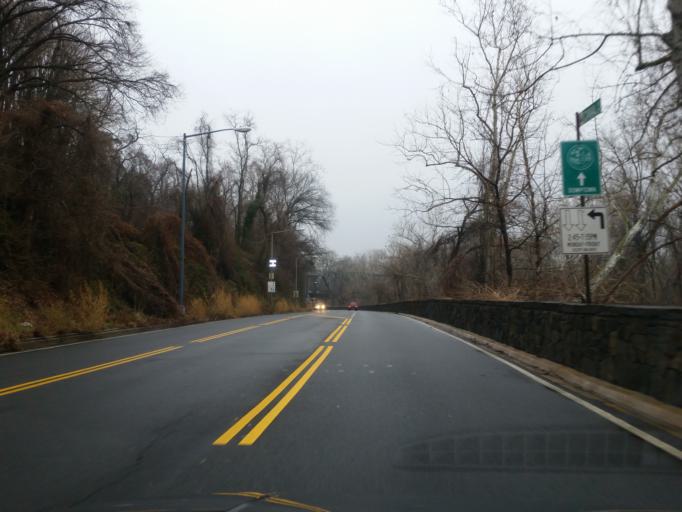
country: US
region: Maryland
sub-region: Montgomery County
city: Brookmont
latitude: 38.9268
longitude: -77.1095
